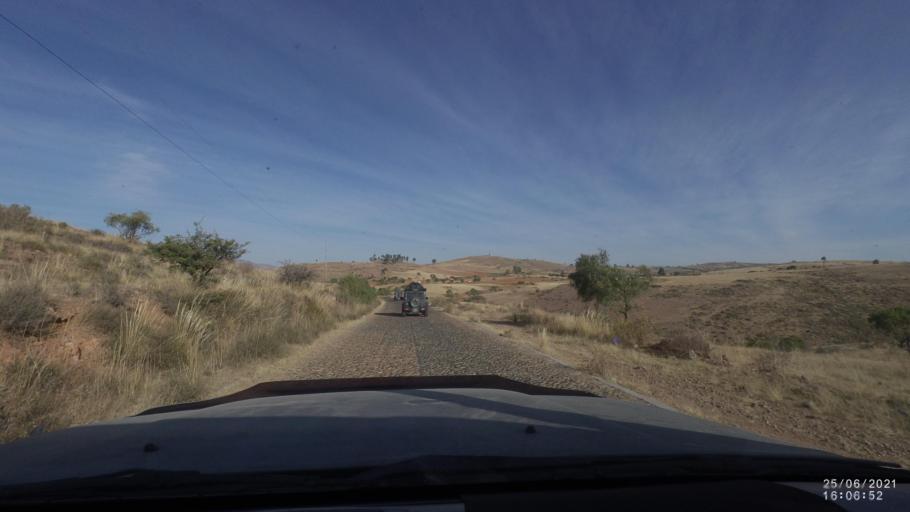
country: BO
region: Cochabamba
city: Cliza
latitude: -17.6690
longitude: -65.9058
